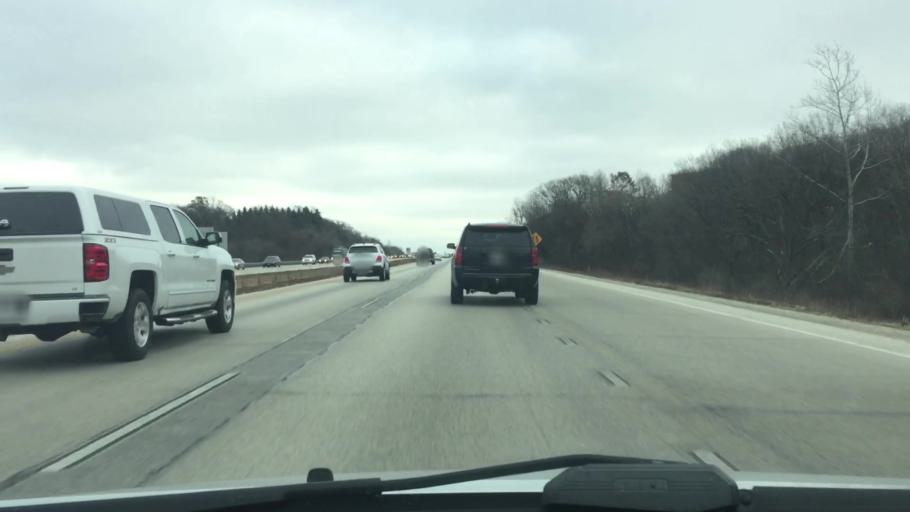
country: US
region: Wisconsin
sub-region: Waukesha County
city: Delafield
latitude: 43.0506
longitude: -88.3671
